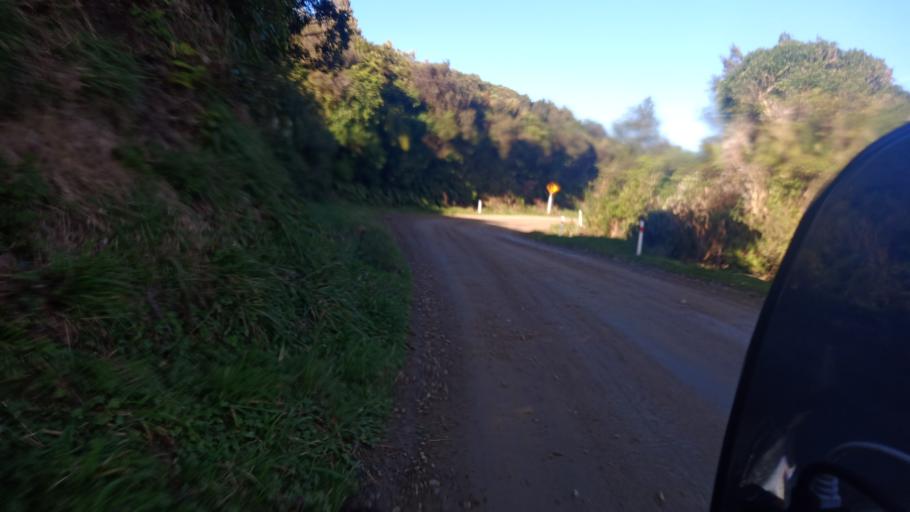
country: NZ
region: Hawke's Bay
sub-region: Wairoa District
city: Wairoa
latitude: -38.7843
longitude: 177.1293
